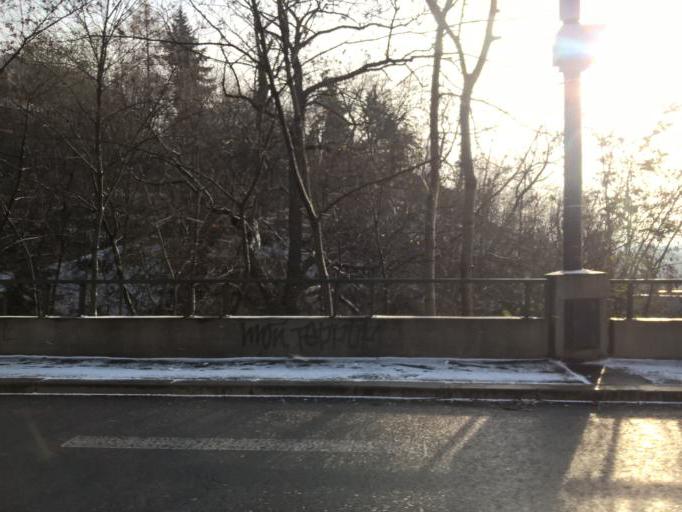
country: CZ
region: Praha
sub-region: Praha 1
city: Mala Strana
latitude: 50.0935
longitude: 14.4092
